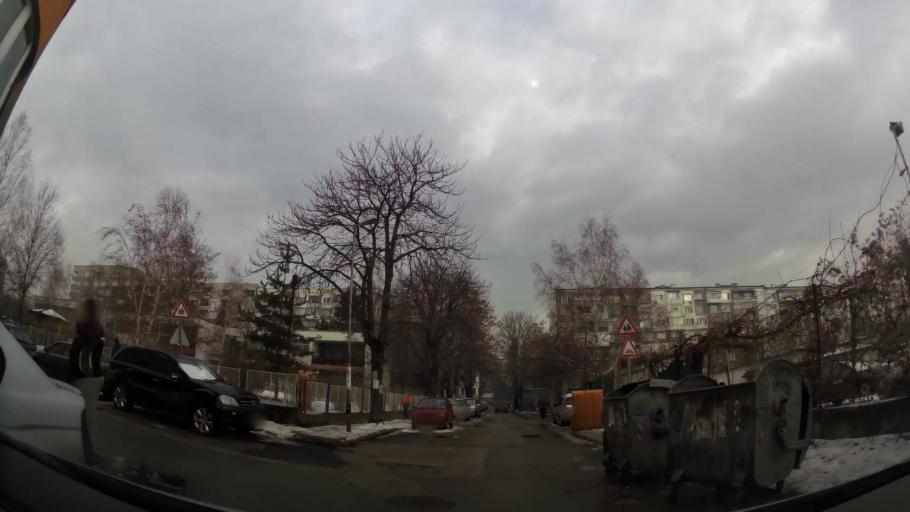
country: BG
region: Sofia-Capital
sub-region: Stolichna Obshtina
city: Sofia
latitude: 42.6920
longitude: 23.2853
